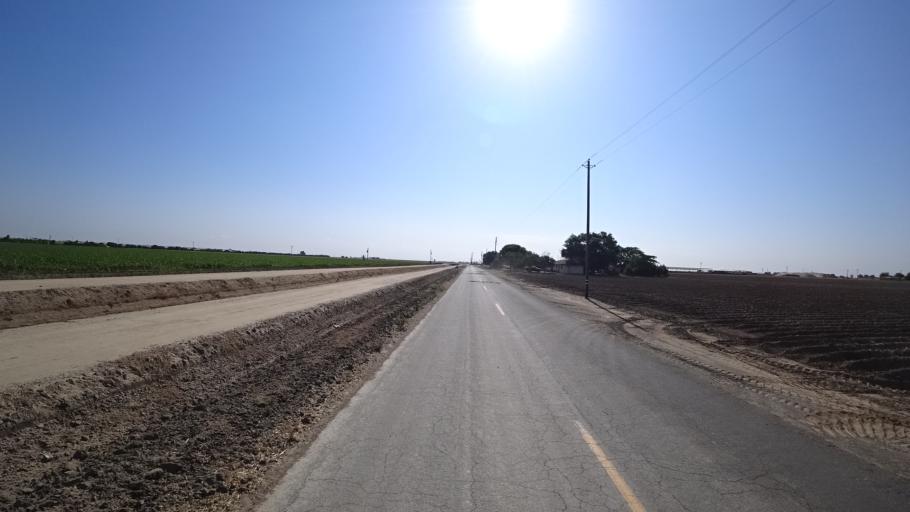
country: US
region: California
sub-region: Kings County
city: Home Garden
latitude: 36.2405
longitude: -119.5776
